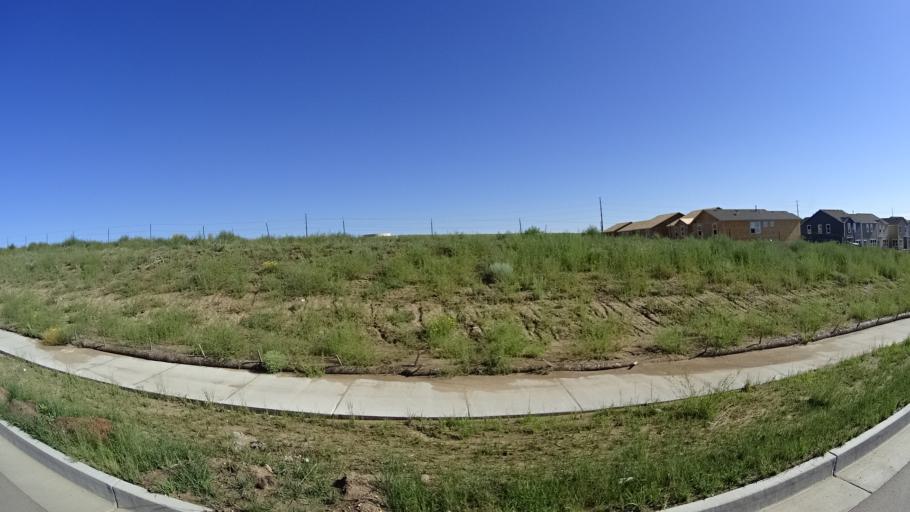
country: US
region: Colorado
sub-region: El Paso County
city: Cimarron Hills
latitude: 38.8969
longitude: -104.6784
